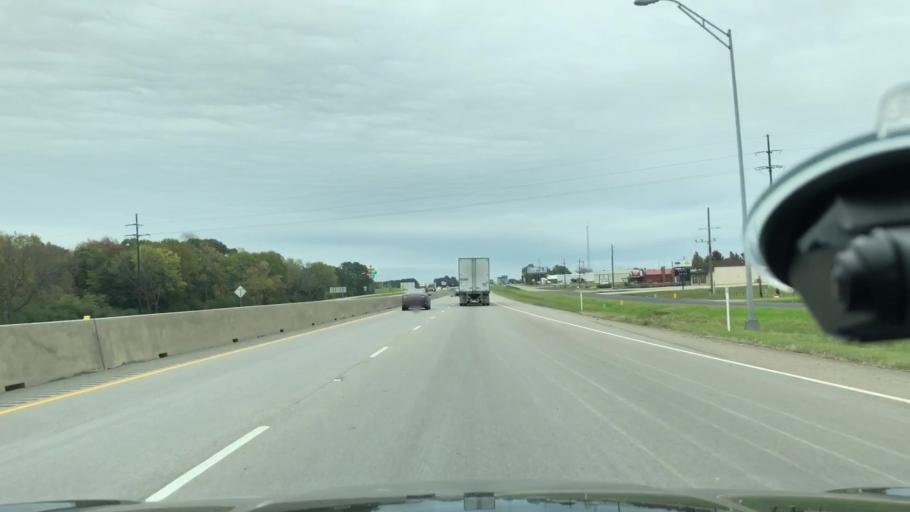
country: US
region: Texas
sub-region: Franklin County
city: Mount Vernon
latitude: 33.1620
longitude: -95.2289
